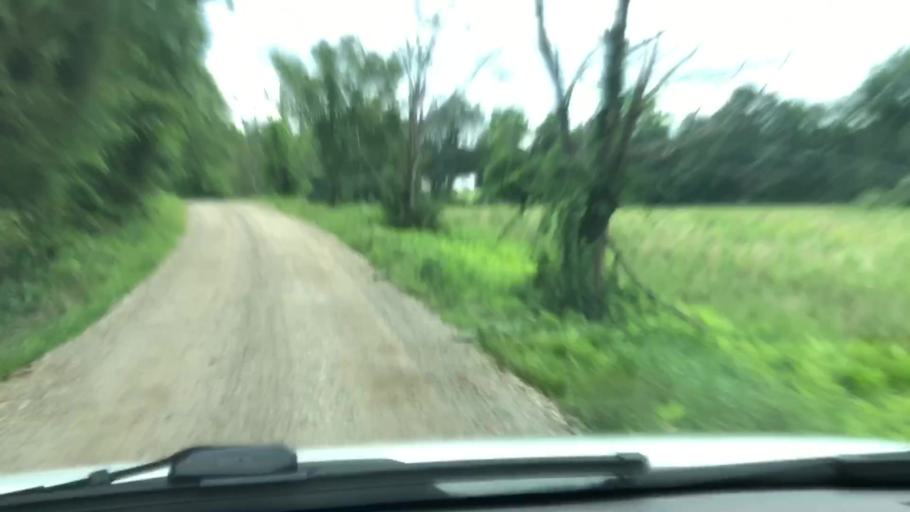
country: US
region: Massachusetts
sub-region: Franklin County
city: South Deerfield
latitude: 42.5258
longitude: -72.5982
